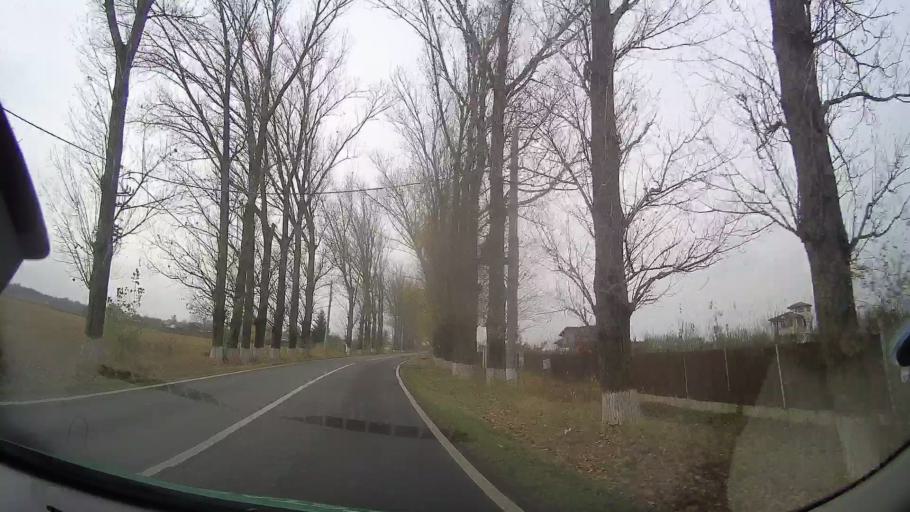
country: RO
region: Ilfov
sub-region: Comuna Gruiu
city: Silistea Snagovului
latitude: 44.7460
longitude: 26.2004
